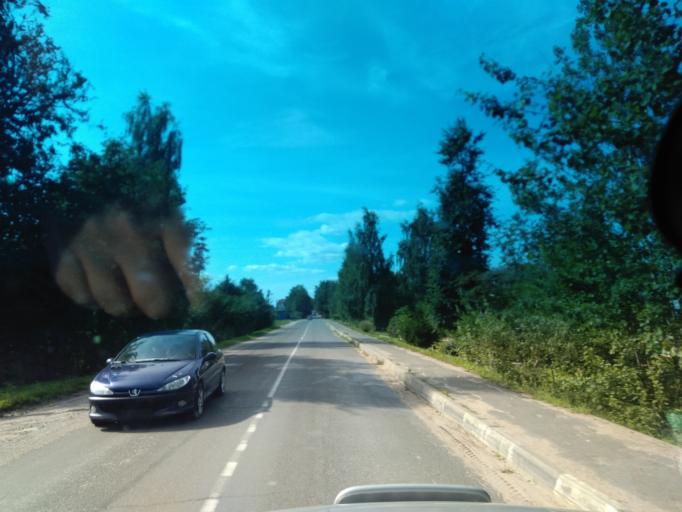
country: BY
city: Fanipol
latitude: 53.7487
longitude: 27.3391
